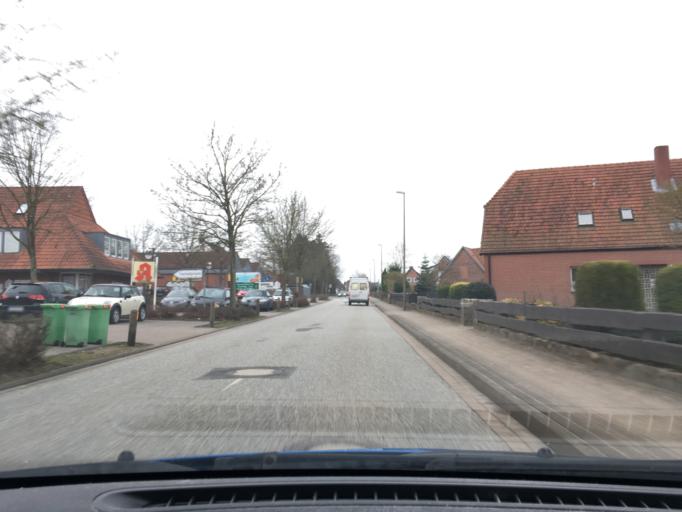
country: DE
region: Lower Saxony
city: Vogelsen
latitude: 53.2767
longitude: 10.3517
